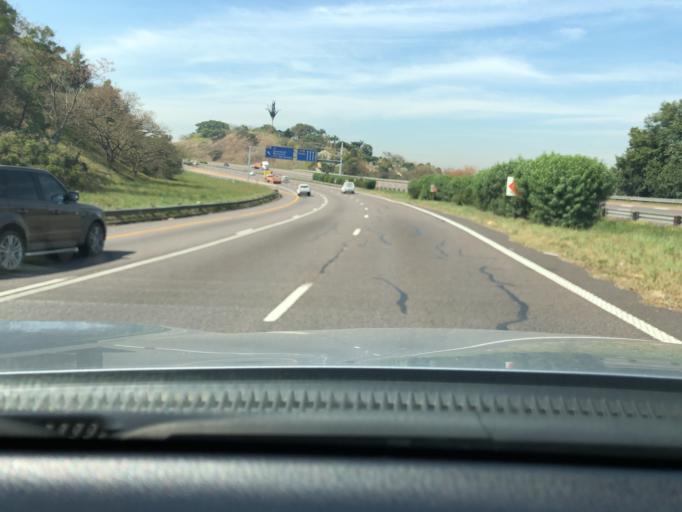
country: ZA
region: KwaZulu-Natal
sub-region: eThekwini Metropolitan Municipality
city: Berea
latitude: -29.8360
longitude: 30.8543
